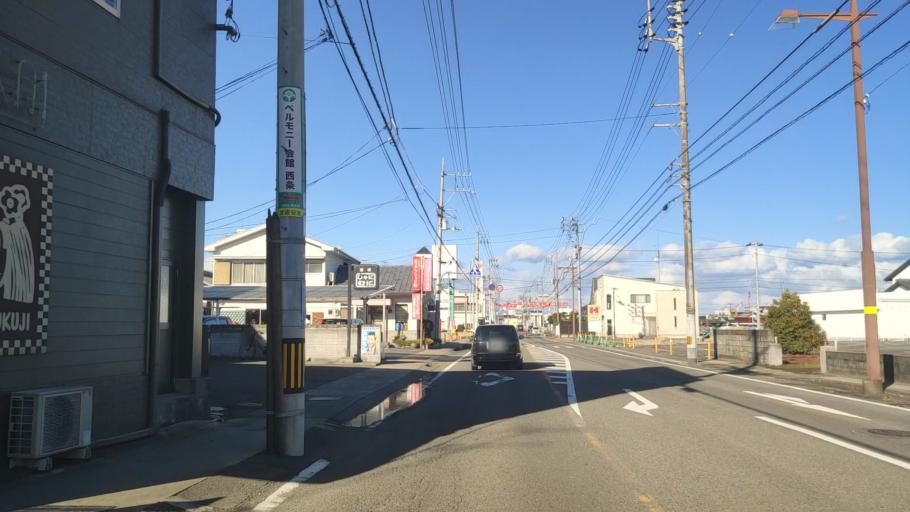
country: JP
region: Ehime
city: Saijo
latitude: 33.9187
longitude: 133.1918
